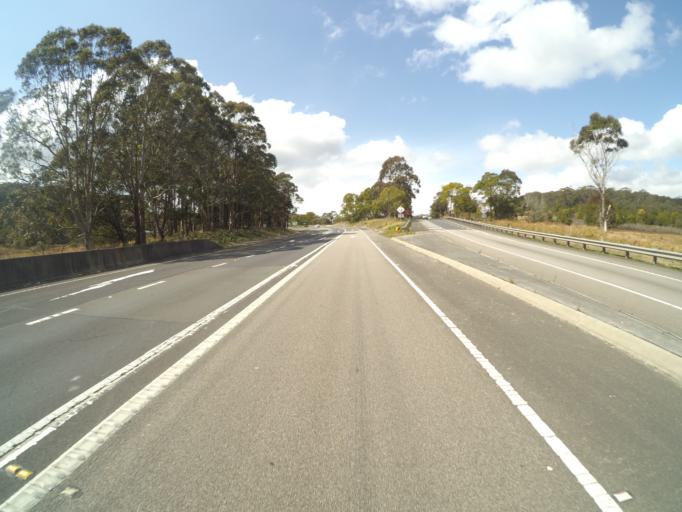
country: AU
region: New South Wales
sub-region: Wollongong
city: Mount Ousley
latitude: -34.3638
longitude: 150.8548
